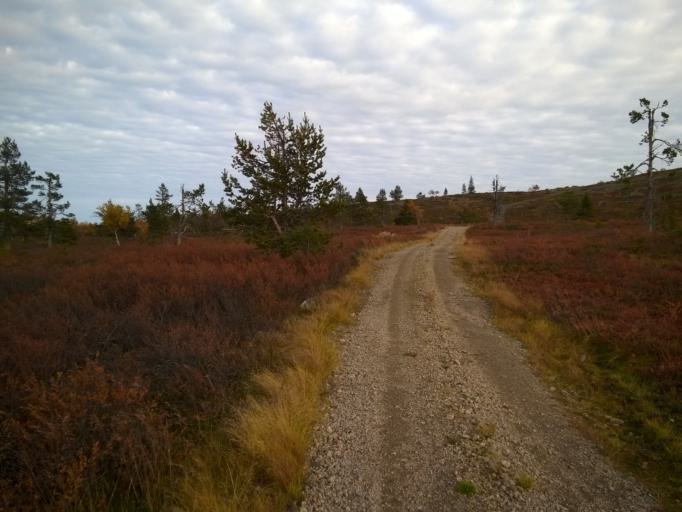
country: FI
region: Lapland
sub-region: Tunturi-Lappi
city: Muonio
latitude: 67.9815
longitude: 24.1152
